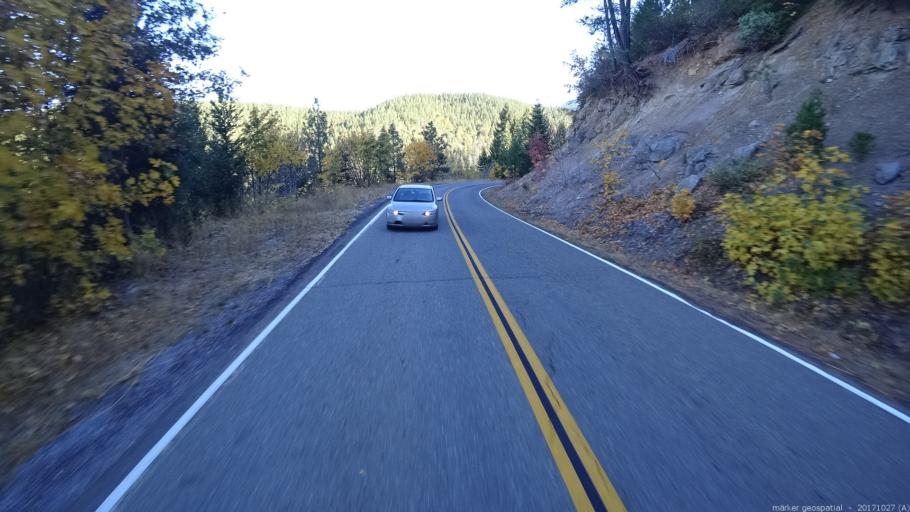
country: US
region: California
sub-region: Shasta County
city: Burney
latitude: 40.8708
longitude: -121.8990
